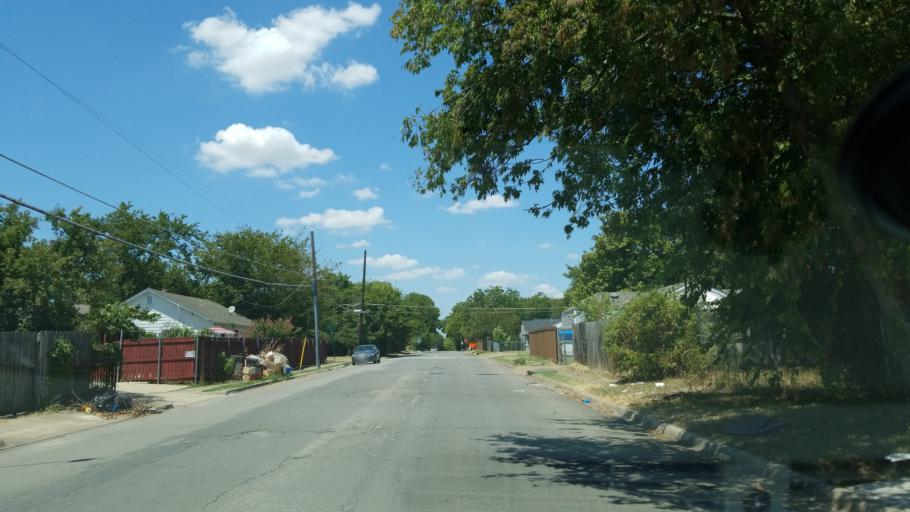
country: US
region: Texas
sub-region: Dallas County
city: Cockrell Hill
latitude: 32.7268
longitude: -96.8851
